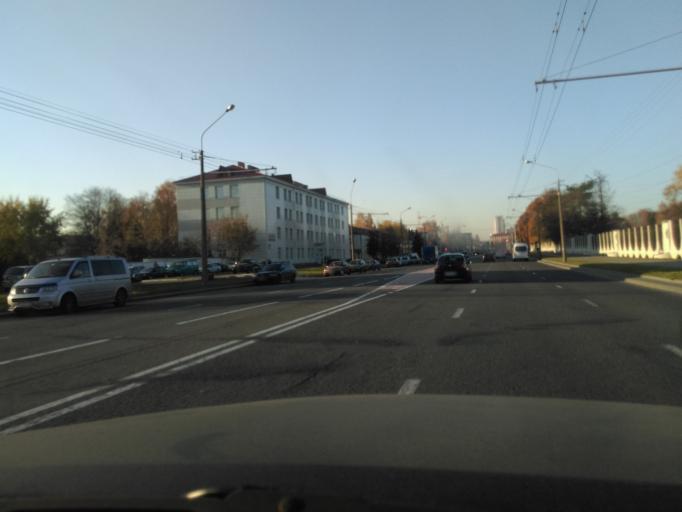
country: BY
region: Minsk
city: Minsk
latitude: 53.9085
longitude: 27.6118
